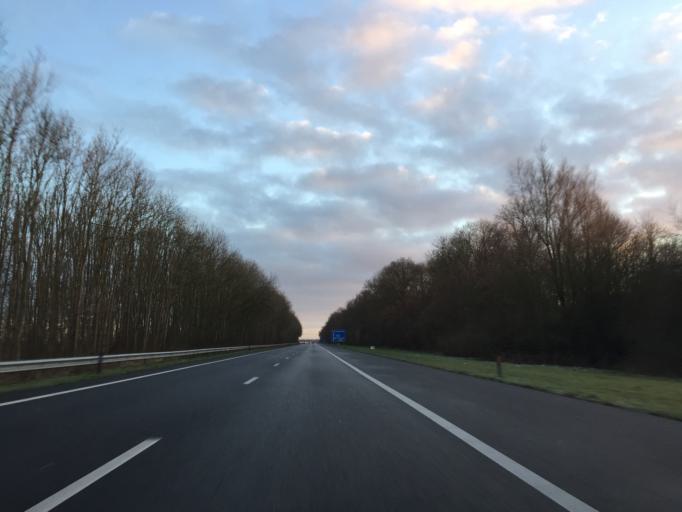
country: NL
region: Flevoland
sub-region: Gemeente Noordoostpolder
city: Emmeloord
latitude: 52.7799
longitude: 5.7591
